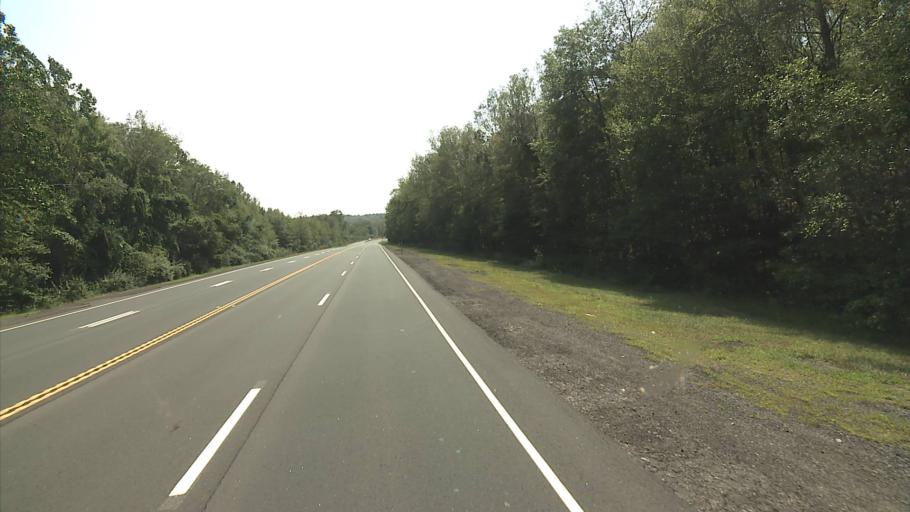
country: US
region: Connecticut
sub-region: Middlesex County
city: East Haddam
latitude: 41.4263
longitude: -72.4906
